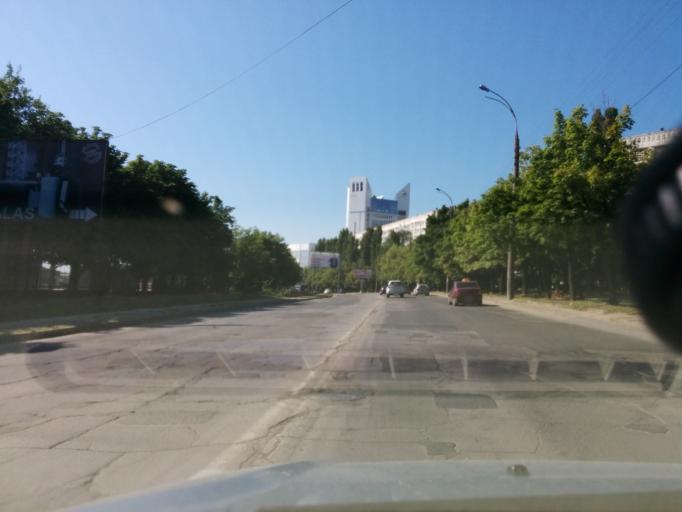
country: MD
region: Chisinau
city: Chisinau
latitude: 47.0187
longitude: 28.8559
